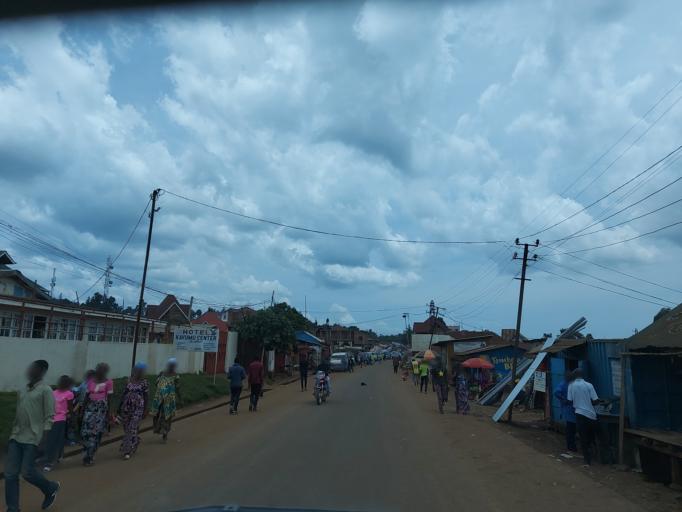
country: CD
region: South Kivu
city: Bukavu
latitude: -2.2978
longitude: 28.7984
